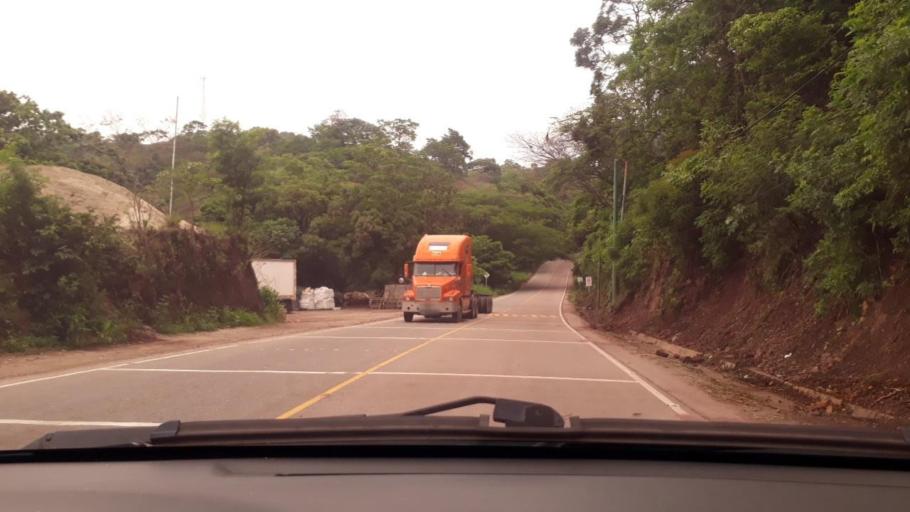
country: GT
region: Chiquimula
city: Concepcion Las Minas
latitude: 14.4676
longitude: -89.4610
